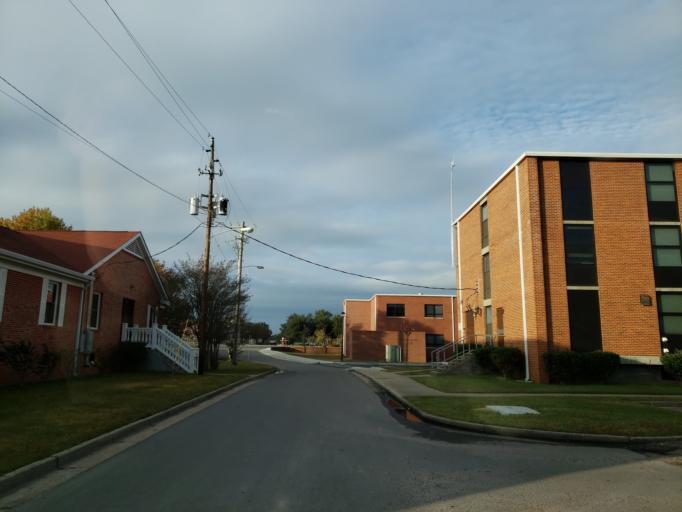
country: US
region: Mississippi
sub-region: Forrest County
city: Hattiesburg
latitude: 31.3035
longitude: -89.2903
